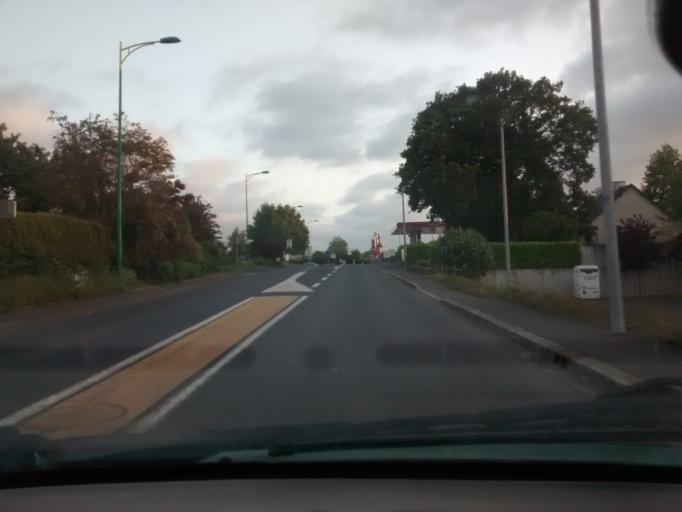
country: FR
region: Lower Normandy
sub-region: Departement de la Manche
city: Agneaux
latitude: 49.1028
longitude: -1.1141
